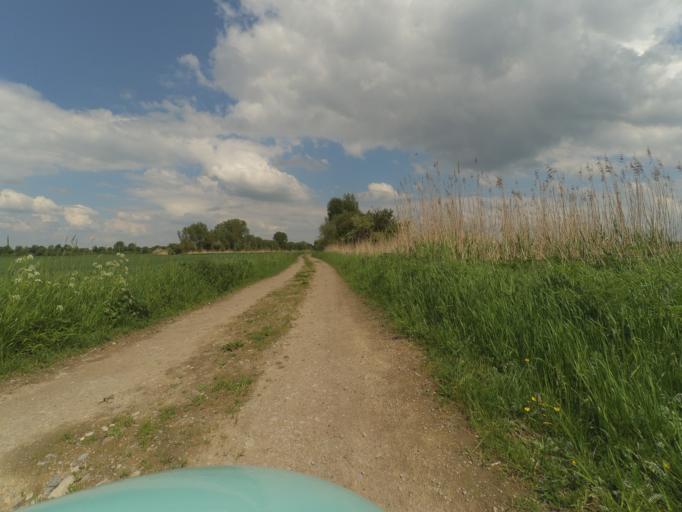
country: DE
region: Lower Saxony
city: Sehnde
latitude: 52.3088
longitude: 9.9234
